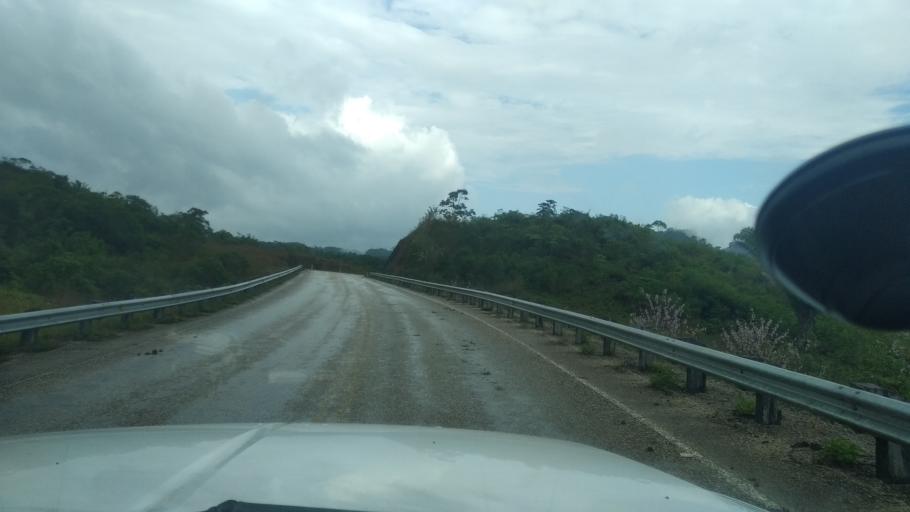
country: GT
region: Peten
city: San Luis
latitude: 16.1882
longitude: -89.1818
